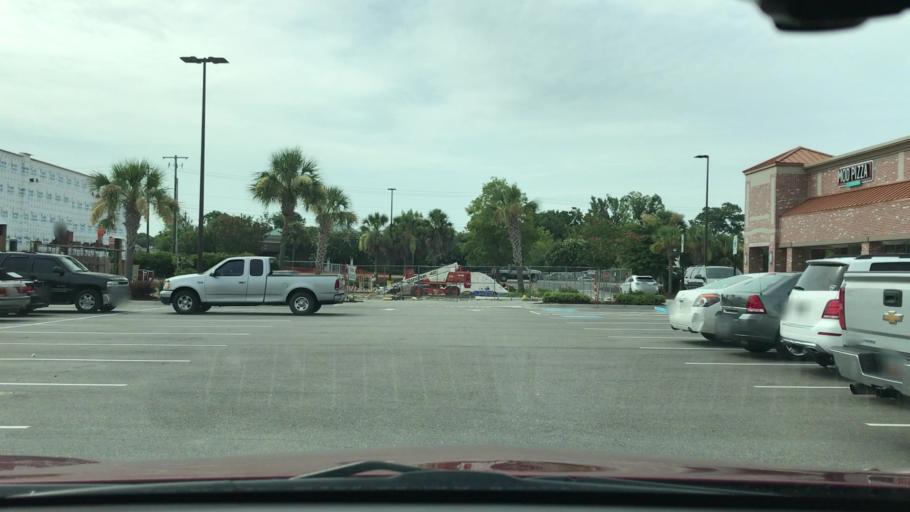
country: US
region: South Carolina
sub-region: Charleston County
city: North Charleston
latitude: 32.8014
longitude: -80.0199
